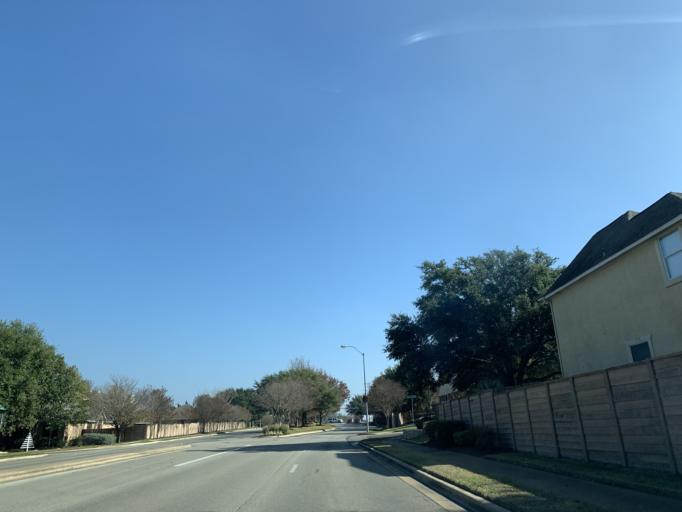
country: US
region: Texas
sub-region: Travis County
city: Windemere
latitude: 30.5083
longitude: -97.6156
